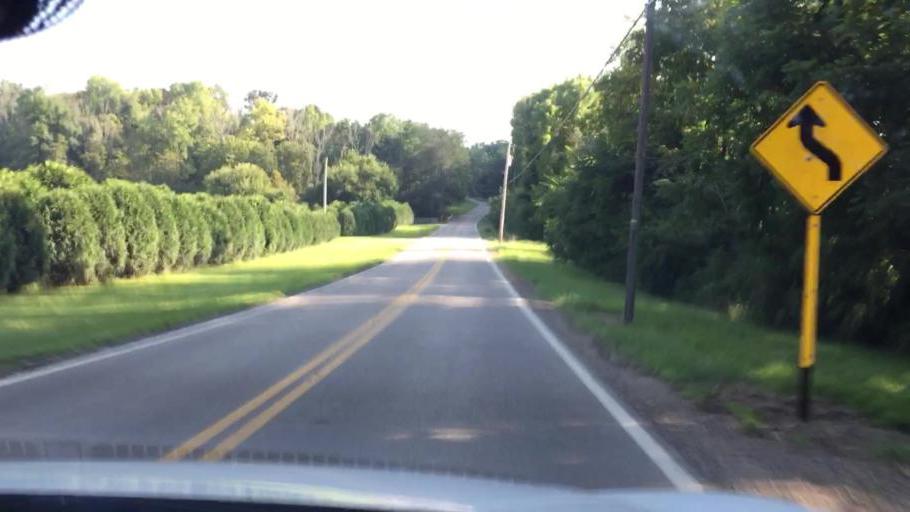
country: US
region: Ohio
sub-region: Clark County
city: Northridge
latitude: 39.9833
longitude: -83.7058
